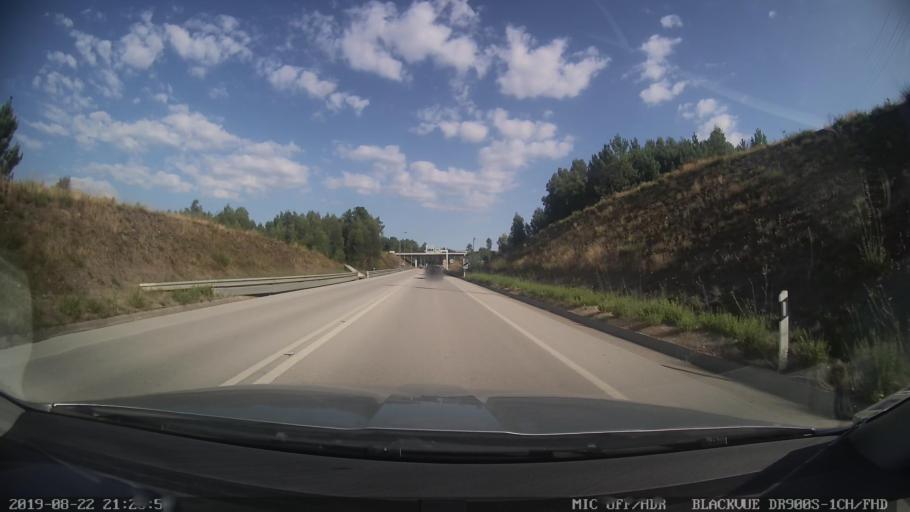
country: PT
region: Castelo Branco
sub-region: Serta
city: Serta
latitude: 39.8592
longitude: -8.1277
